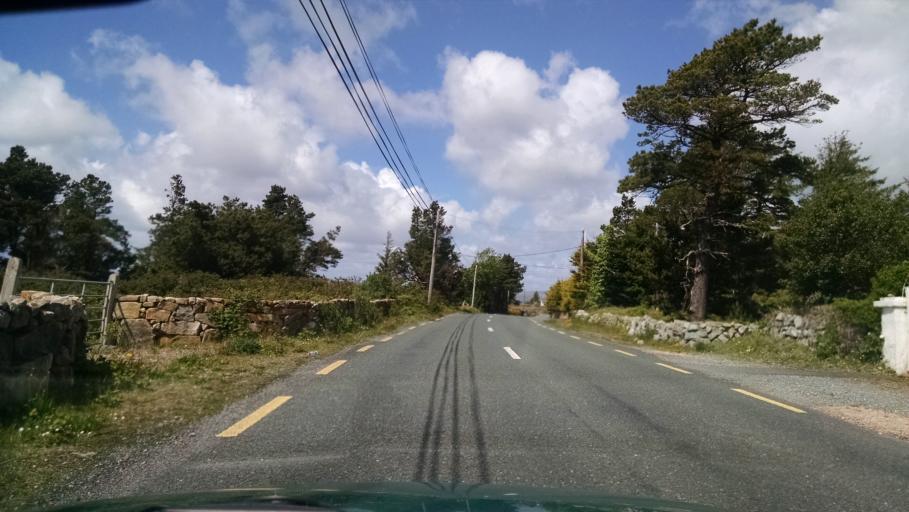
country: IE
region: Connaught
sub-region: County Galway
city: Oughterard
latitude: 53.3028
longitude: -9.5854
